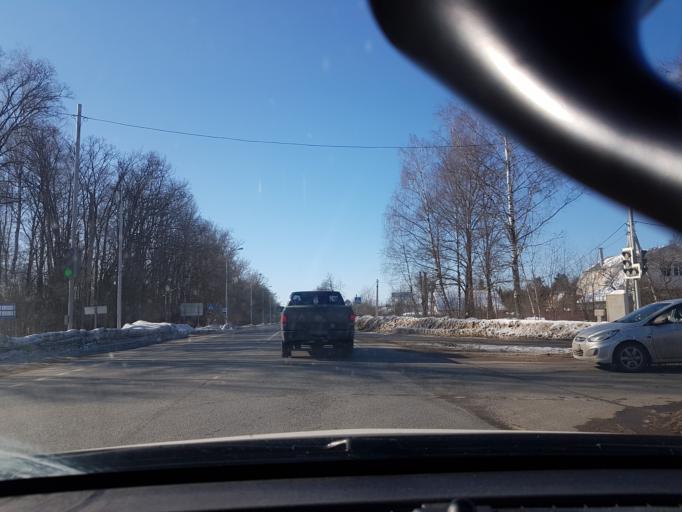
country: RU
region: Moskovskaya
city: Kostrovo
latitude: 55.9156
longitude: 36.6922
